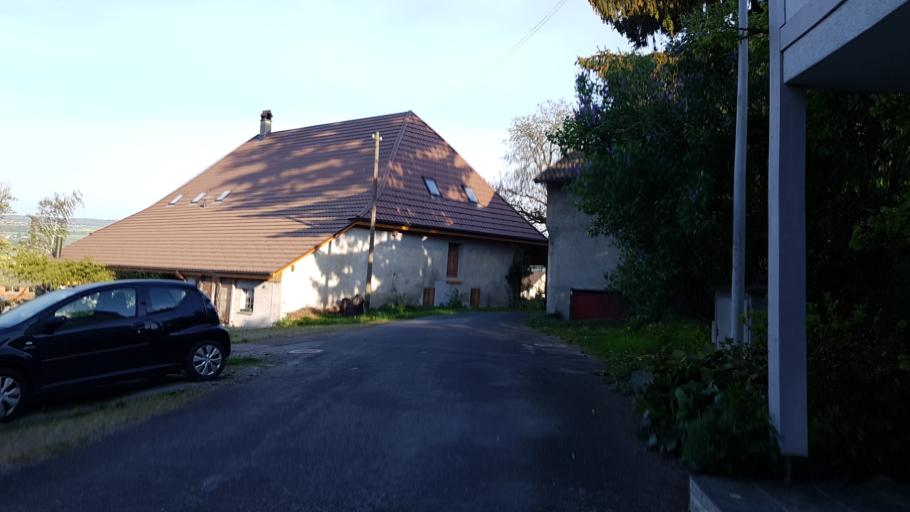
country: CH
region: Aargau
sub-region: Bezirk Kulm
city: Reinach
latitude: 47.2710
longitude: 8.2026
